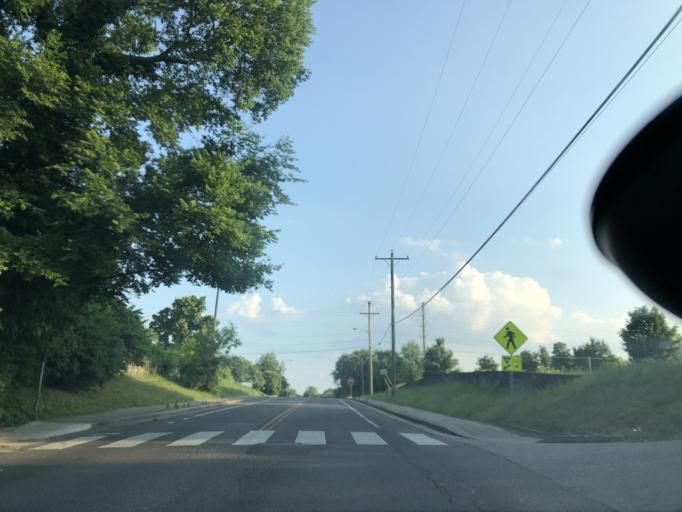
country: US
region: Tennessee
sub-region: Davidson County
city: Oak Hill
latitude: 36.1181
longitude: -86.7913
